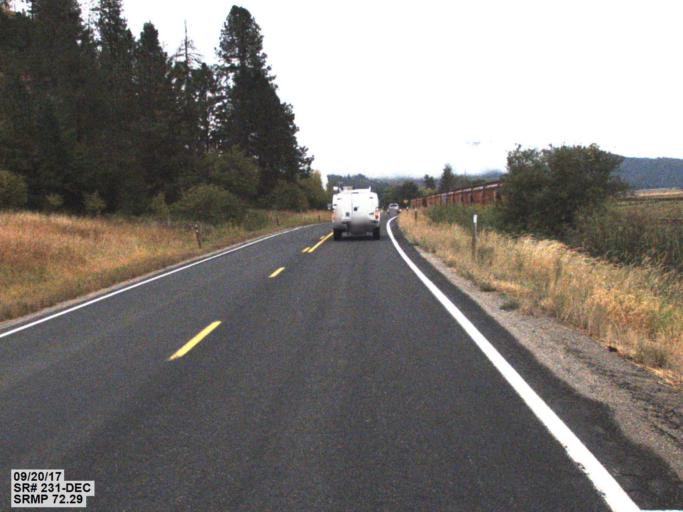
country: US
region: Washington
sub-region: Stevens County
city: Chewelah
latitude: 48.1811
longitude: -117.7297
